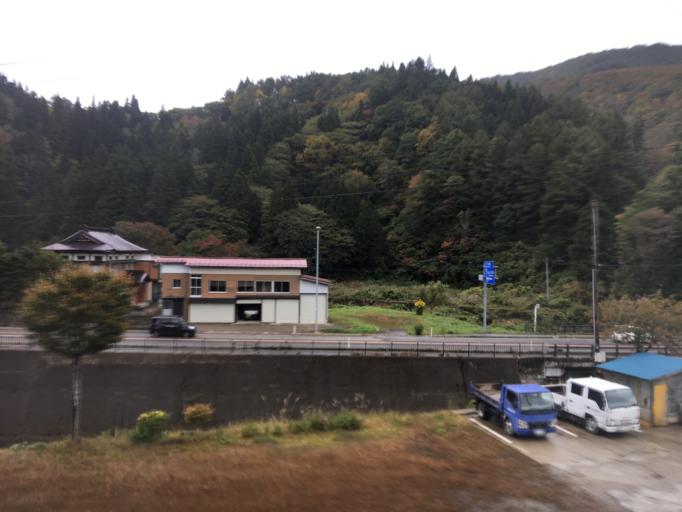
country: JP
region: Yamagata
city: Nagai
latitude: 38.0228
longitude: 139.8792
